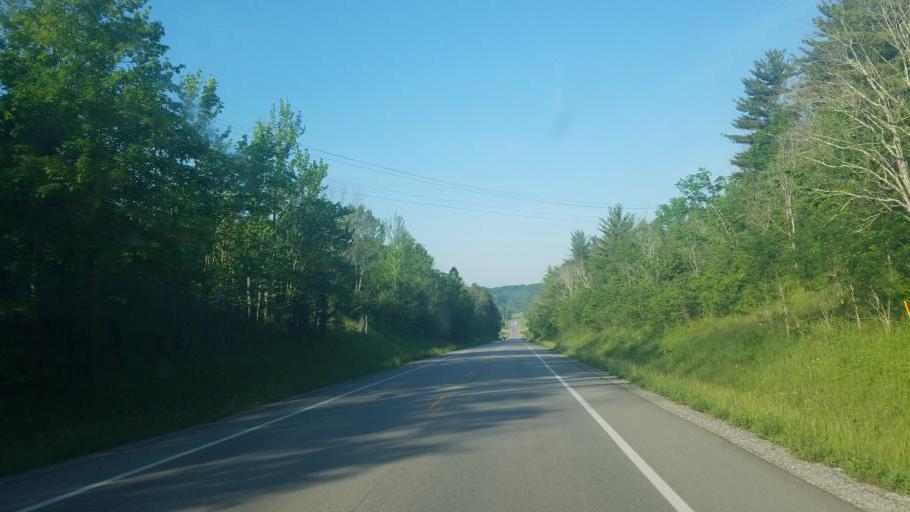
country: US
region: West Virginia
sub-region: Mason County
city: New Haven
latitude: 39.1294
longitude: -81.8752
